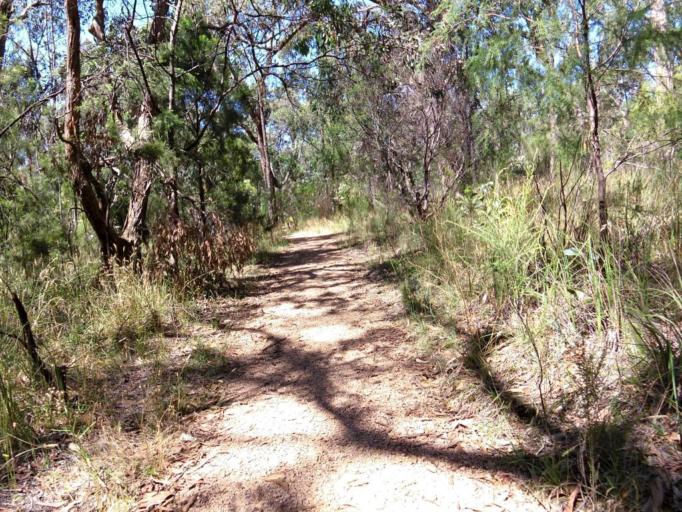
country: AU
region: Victoria
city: Mitcham
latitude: -37.8143
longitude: 145.2083
